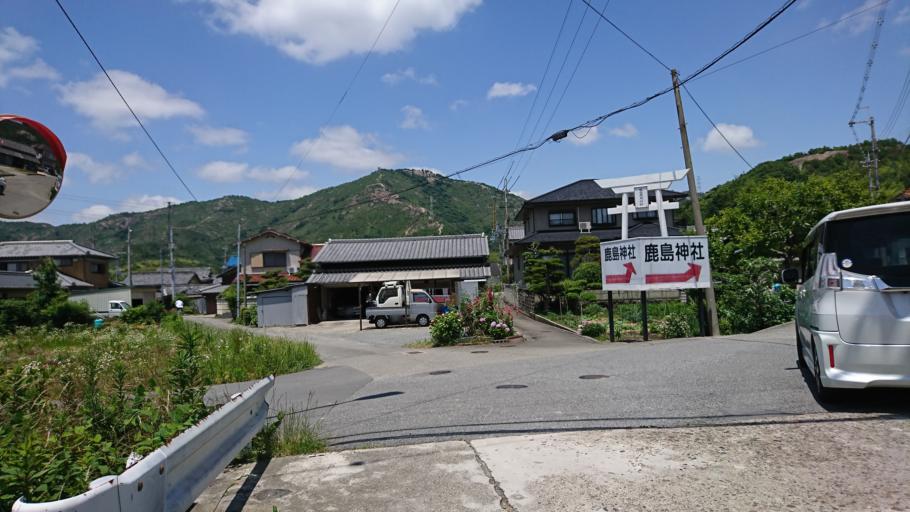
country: JP
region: Hyogo
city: Kakogawacho-honmachi
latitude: 34.8009
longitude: 134.7899
